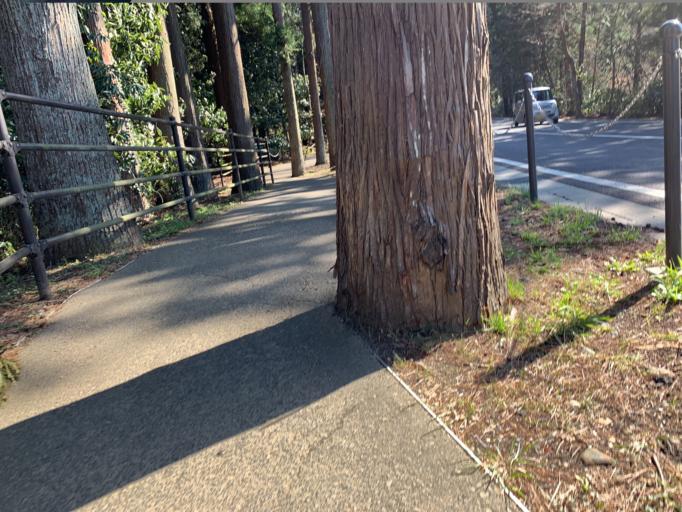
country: JP
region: Miyagi
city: Sendai
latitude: 38.2565
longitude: 140.8559
